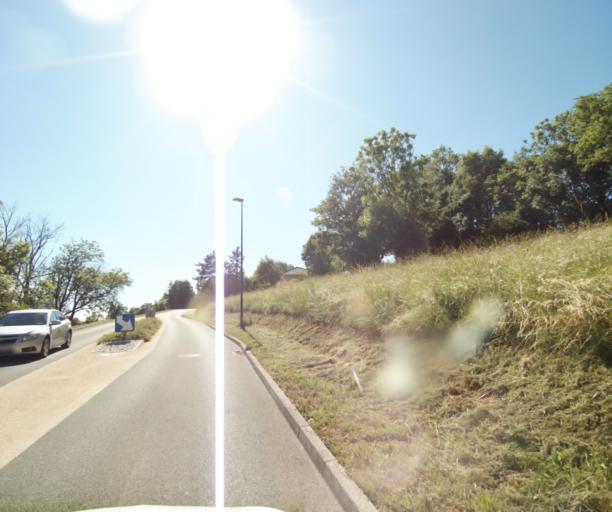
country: FR
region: Rhone-Alpes
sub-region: Departement de la Haute-Savoie
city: Ballaison
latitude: 46.2970
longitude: 6.3627
